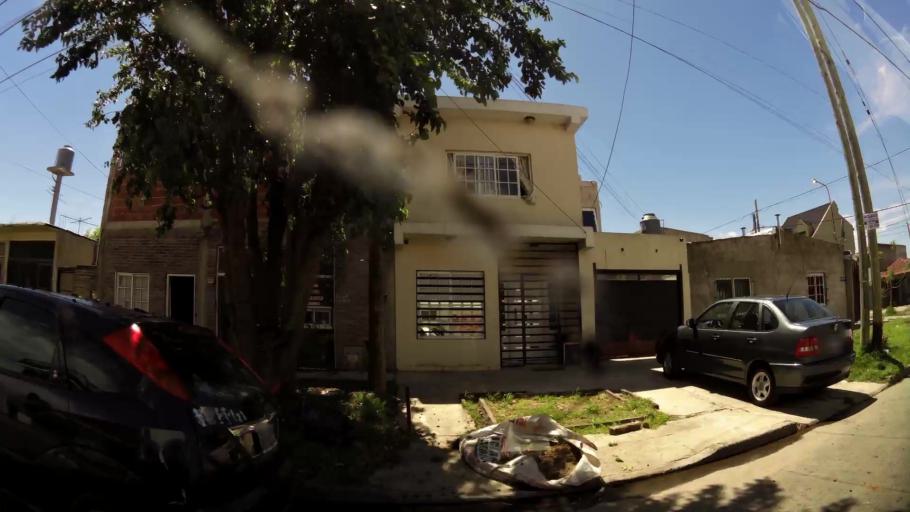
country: AR
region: Buenos Aires
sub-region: Partido de Quilmes
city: Quilmes
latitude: -34.7364
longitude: -58.3000
